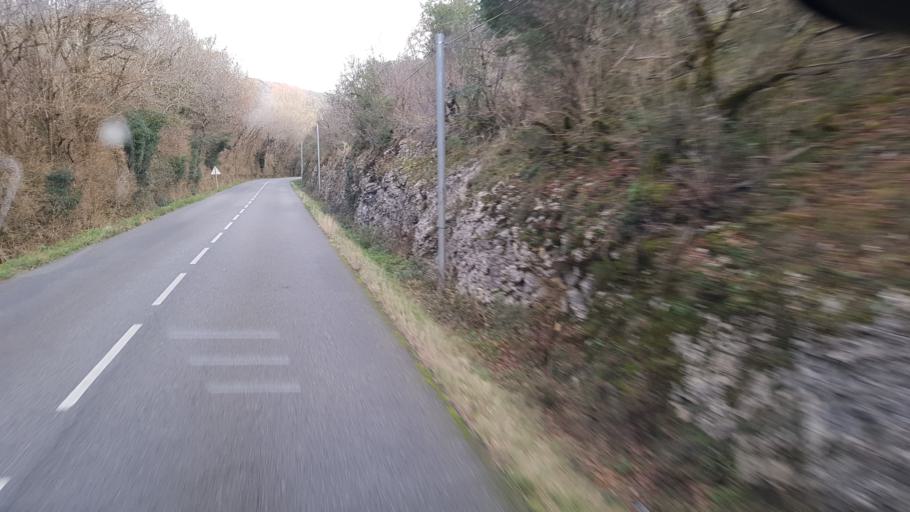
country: FR
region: Midi-Pyrenees
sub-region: Departement du Tarn-et-Garonne
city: Montricoux
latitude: 44.0328
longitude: 1.6695
